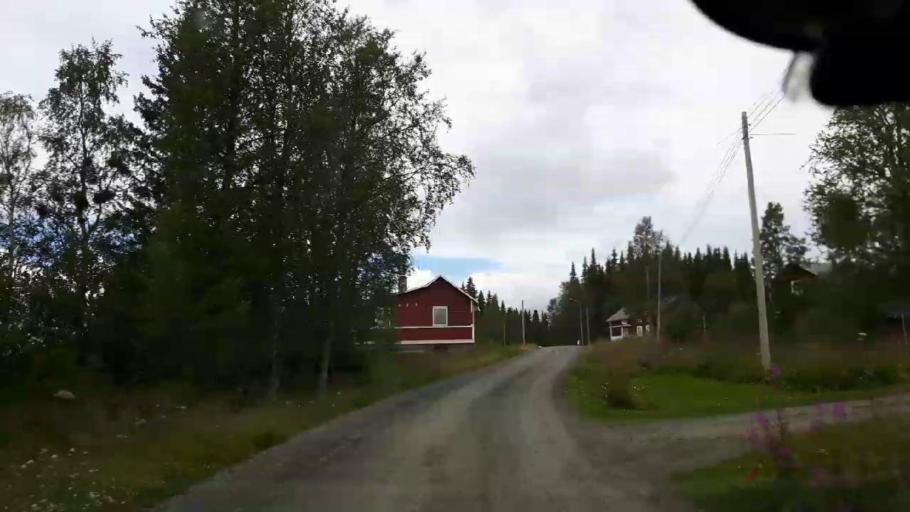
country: SE
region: Jaemtland
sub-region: Krokoms Kommun
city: Valla
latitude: 63.7056
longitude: 13.8678
